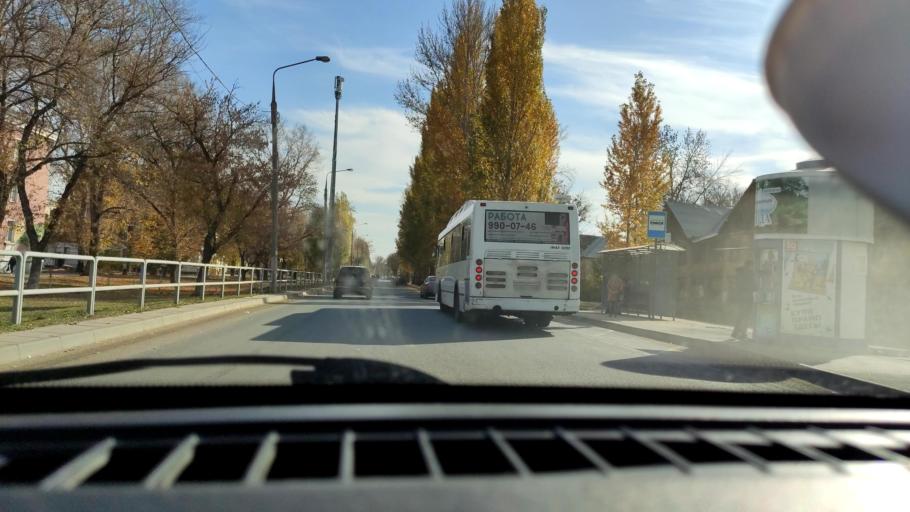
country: RU
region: Samara
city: Petra-Dubrava
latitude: 53.3035
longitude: 50.2820
